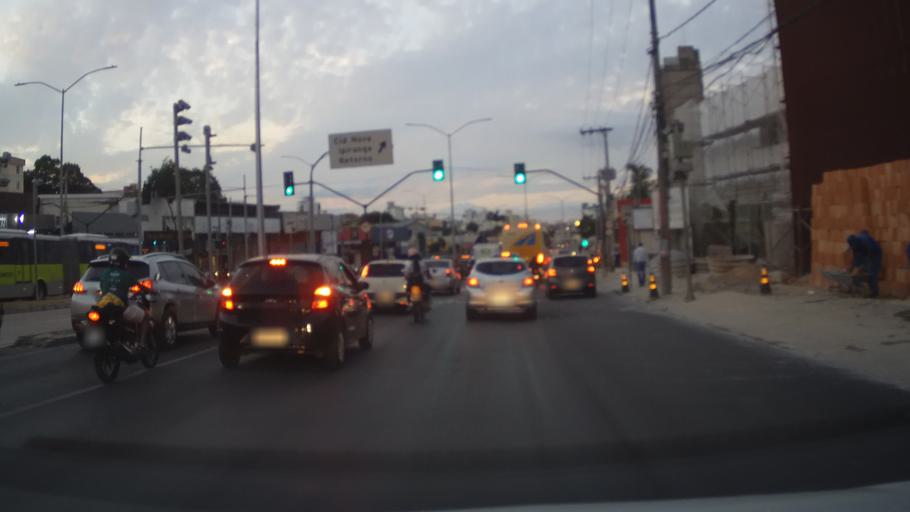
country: BR
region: Minas Gerais
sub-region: Belo Horizonte
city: Belo Horizonte
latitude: -19.8890
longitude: -43.9291
